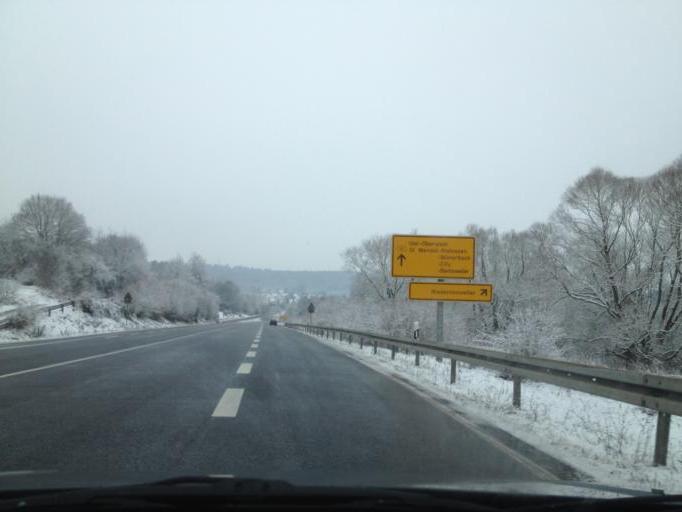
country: DE
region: Saarland
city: Ottweiler
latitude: 49.4217
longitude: 7.1612
